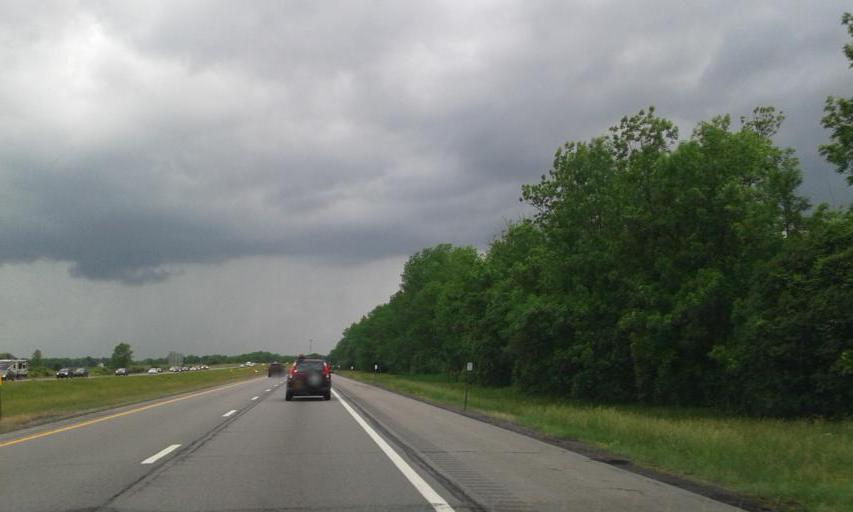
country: US
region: New York
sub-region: Ontario County
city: Manchester
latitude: 42.9794
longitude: -77.2545
